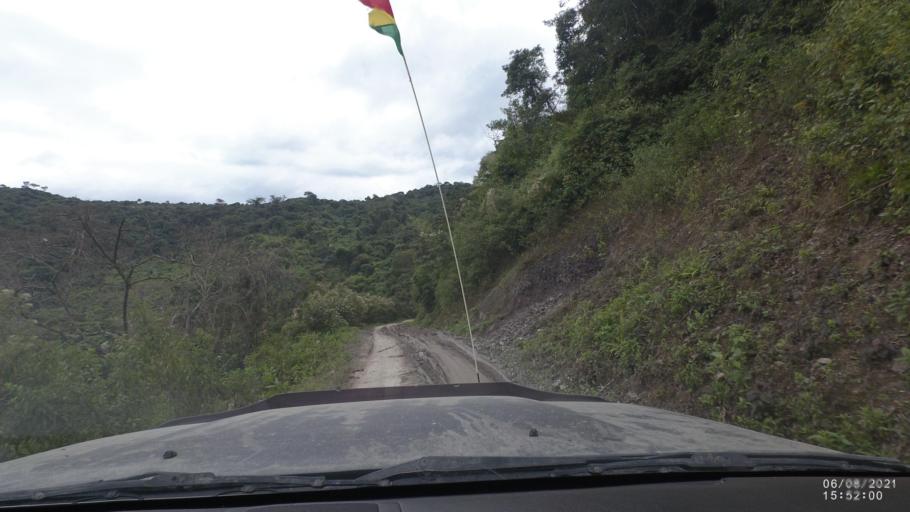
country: BO
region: La Paz
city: Quime
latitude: -16.5872
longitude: -66.7097
